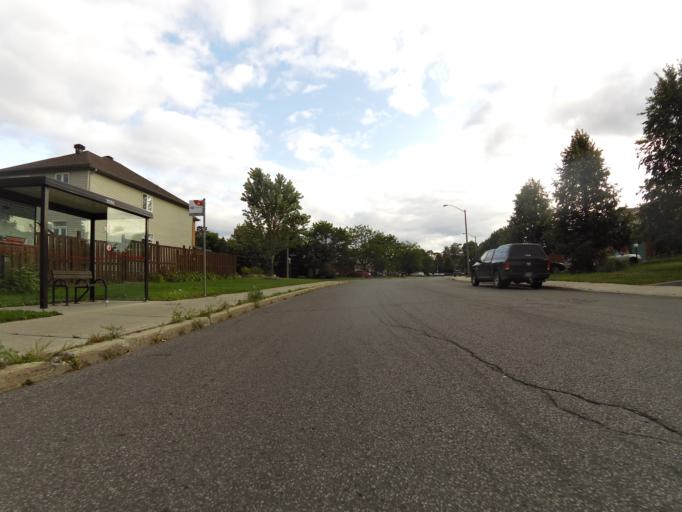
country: CA
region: Ontario
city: Bells Corners
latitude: 45.2858
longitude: -75.7308
